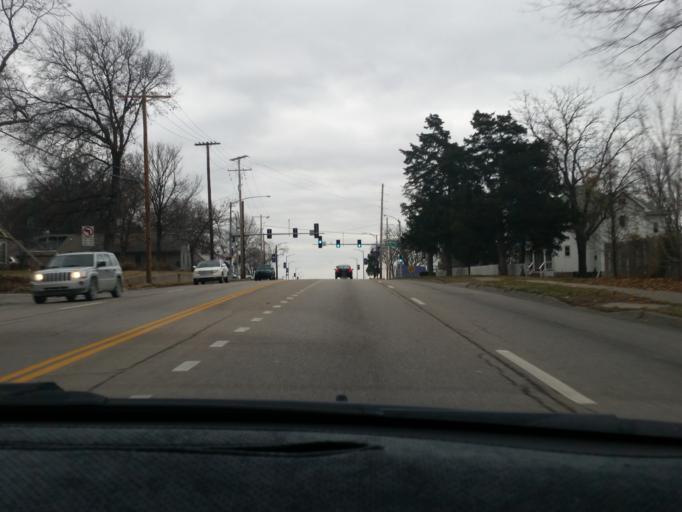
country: US
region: Kansas
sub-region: Douglas County
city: Lawrence
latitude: 38.9428
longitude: -95.2340
